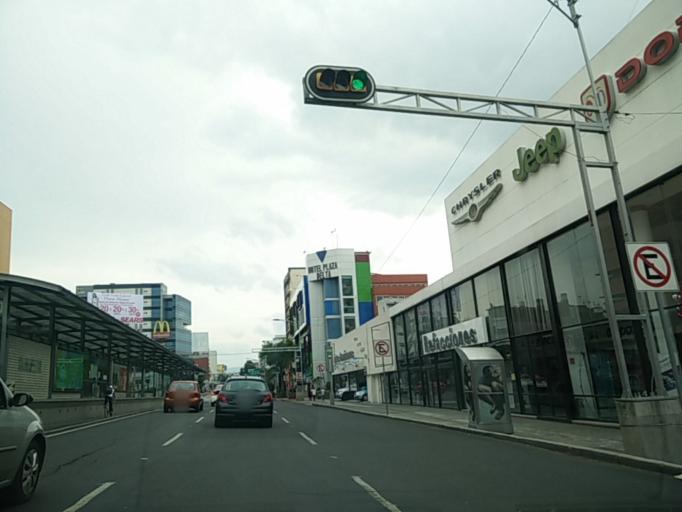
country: MX
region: Mexico City
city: Benito Juarez
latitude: 19.4016
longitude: -99.1557
